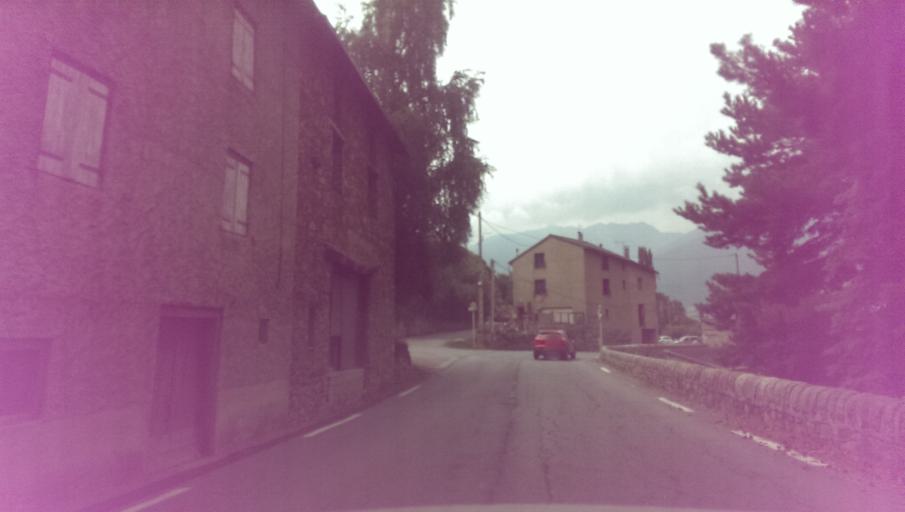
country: ES
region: Catalonia
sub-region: Provincia de Girona
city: Llivia
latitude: 42.5106
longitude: 2.1291
